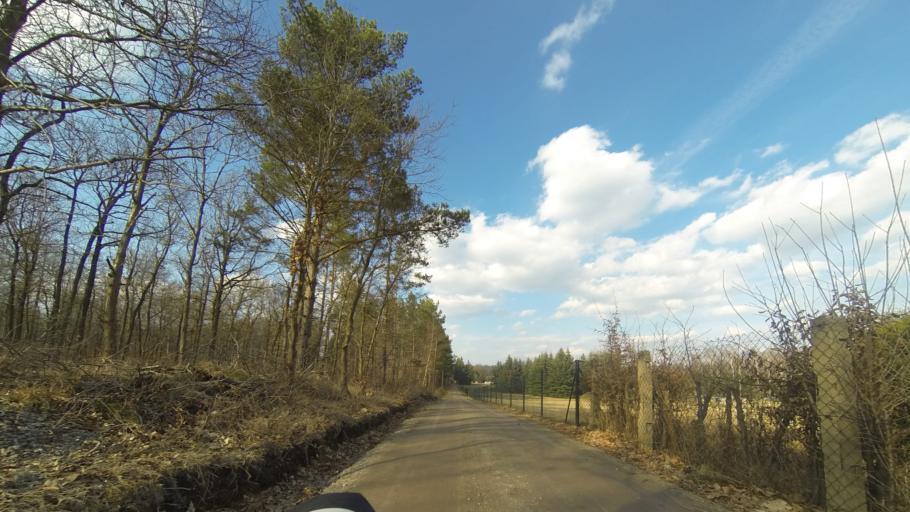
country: DE
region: Saxony
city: Radebeul
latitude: 51.1355
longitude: 13.6286
